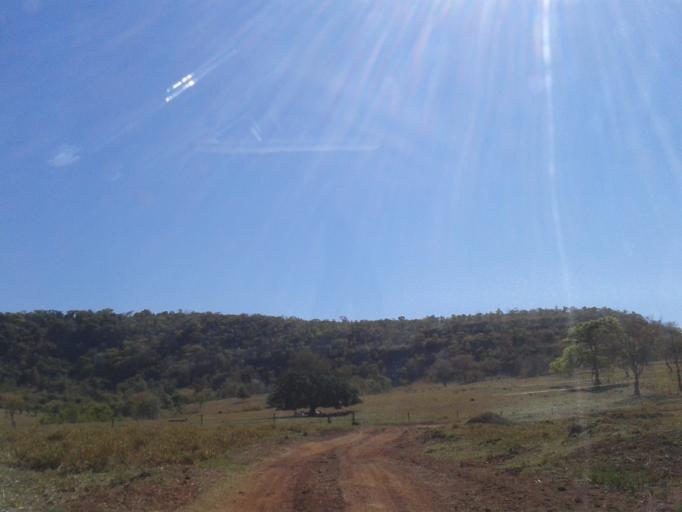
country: BR
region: Minas Gerais
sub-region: Santa Vitoria
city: Santa Vitoria
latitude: -19.1017
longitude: -49.9801
